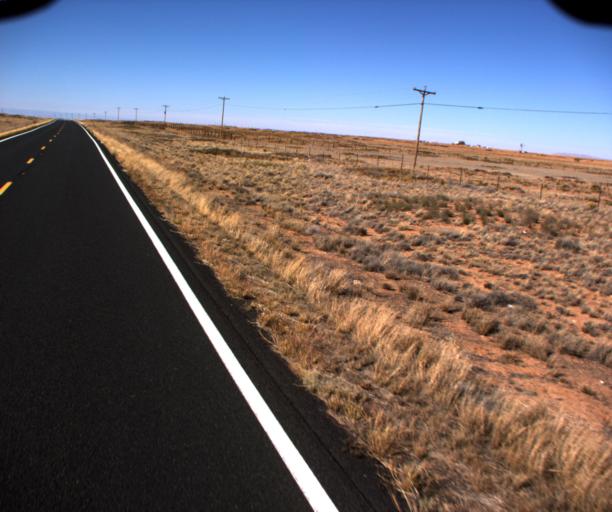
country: US
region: Arizona
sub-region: Coconino County
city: Tuba City
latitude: 36.0036
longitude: -111.0443
